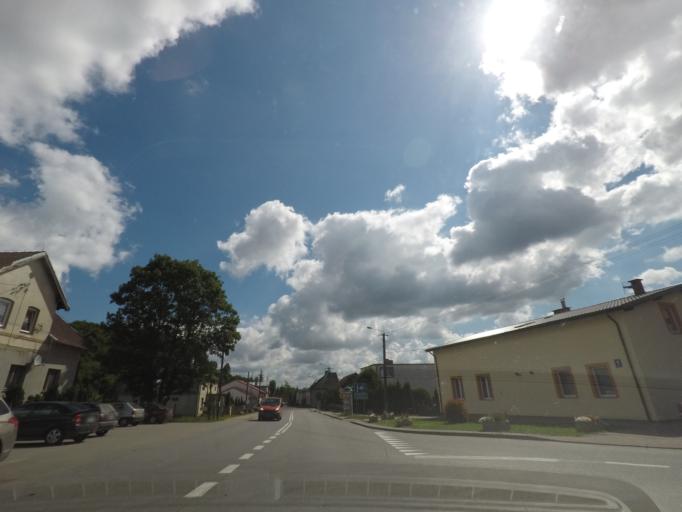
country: PL
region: Pomeranian Voivodeship
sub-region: Powiat wejherowski
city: Leczyce
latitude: 54.5941
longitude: 17.8587
